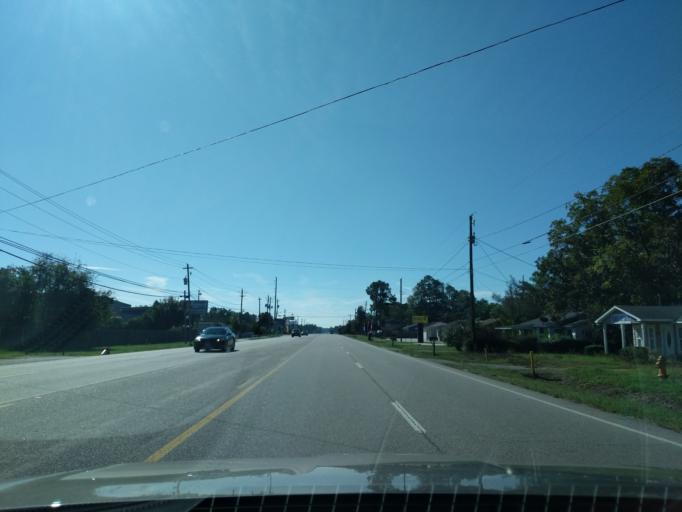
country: US
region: Georgia
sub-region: Richmond County
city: Augusta
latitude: 33.4102
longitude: -82.0066
